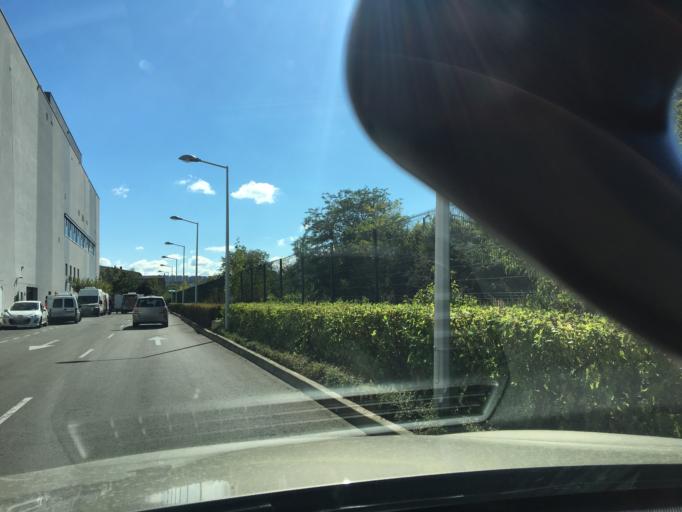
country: BG
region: Burgas
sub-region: Obshtina Burgas
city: Burgas
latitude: 42.5123
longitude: 27.4534
